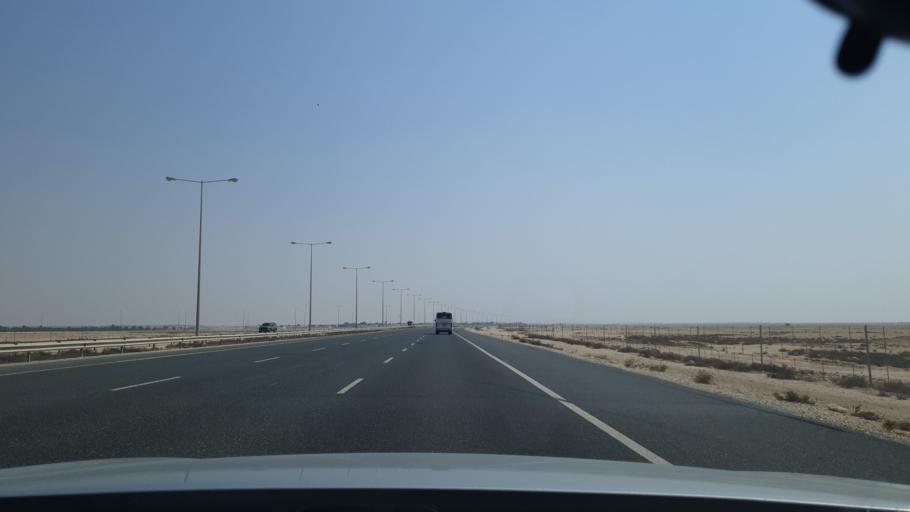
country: QA
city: Al Ghuwayriyah
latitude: 25.8251
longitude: 51.3593
